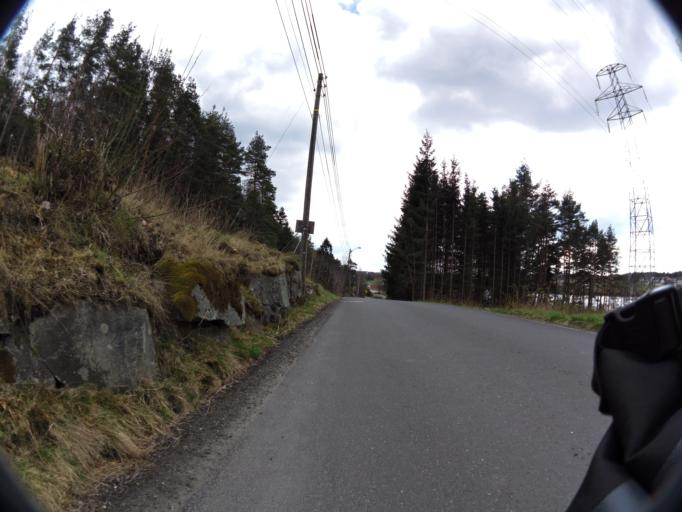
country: NO
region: Ostfold
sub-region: Sarpsborg
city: Sarpsborg
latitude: 59.2775
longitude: 11.0260
